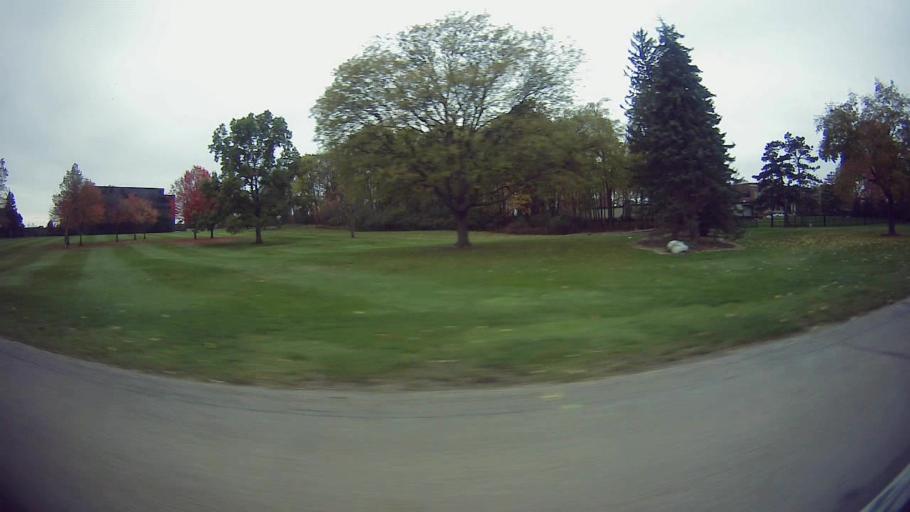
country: US
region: Michigan
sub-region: Oakland County
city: Pontiac
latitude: 42.6546
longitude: -83.3293
